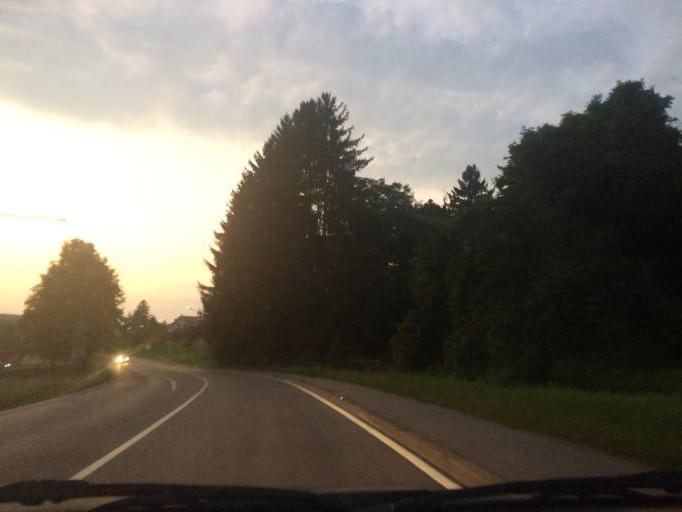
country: DE
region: Baden-Wuerttemberg
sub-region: Regierungsbezirk Stuttgart
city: Schorndorf
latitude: 48.8255
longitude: 9.5202
